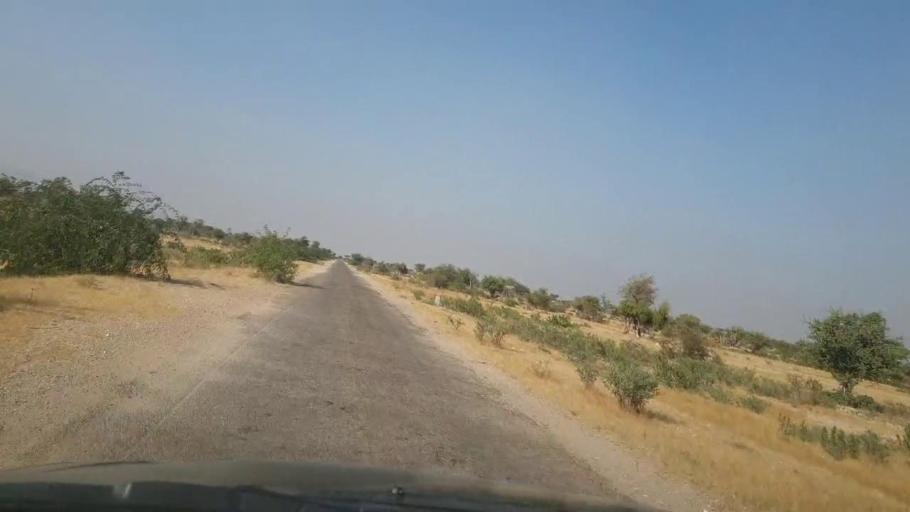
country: PK
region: Sindh
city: Jamshoro
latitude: 25.5627
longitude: 67.8262
